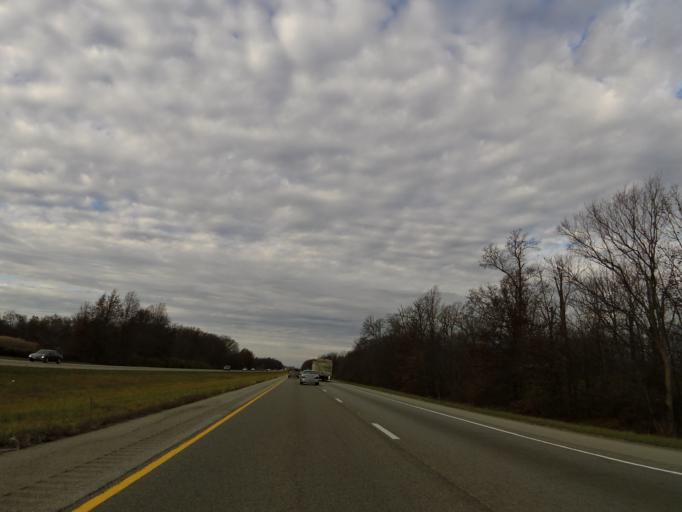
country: US
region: Illinois
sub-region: Clinton County
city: Wamac
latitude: 38.3872
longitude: -89.1391
